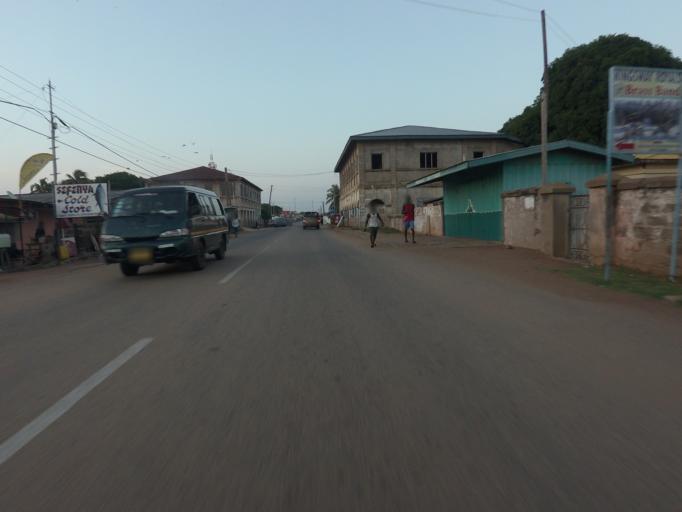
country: GH
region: Volta
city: Keta
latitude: 5.8885
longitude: 0.9835
